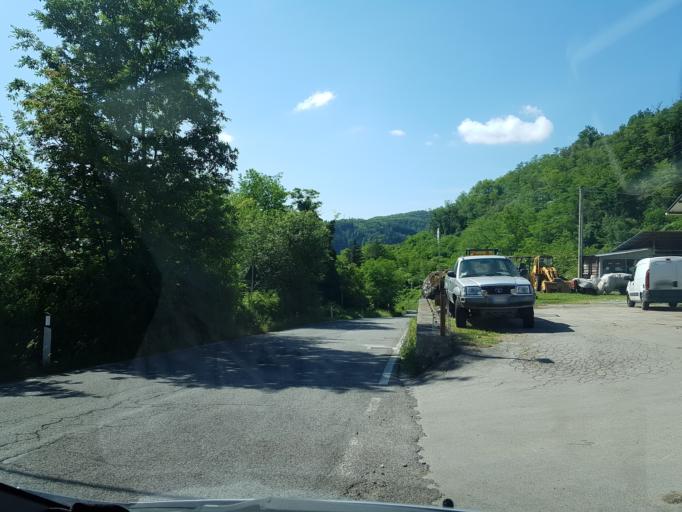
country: IT
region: Tuscany
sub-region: Provincia di Lucca
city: Camporgiano
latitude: 44.1533
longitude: 10.3427
